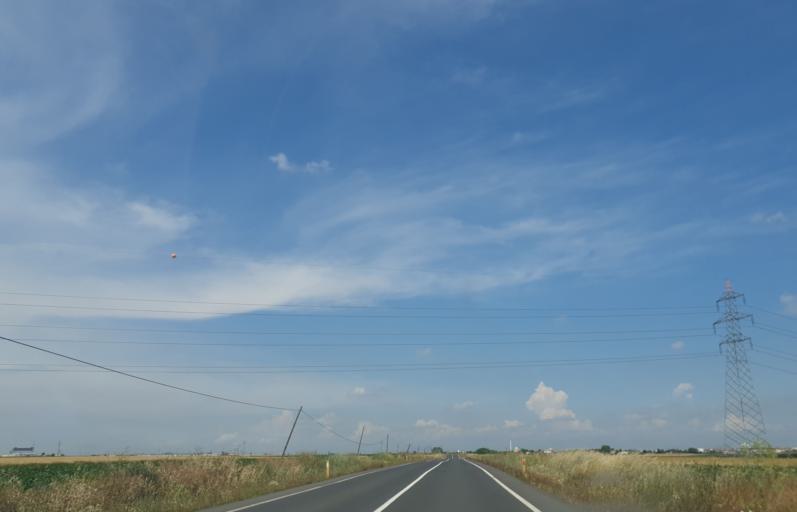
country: TR
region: Kirklareli
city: Buyukkaristiran
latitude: 41.2521
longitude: 27.6232
